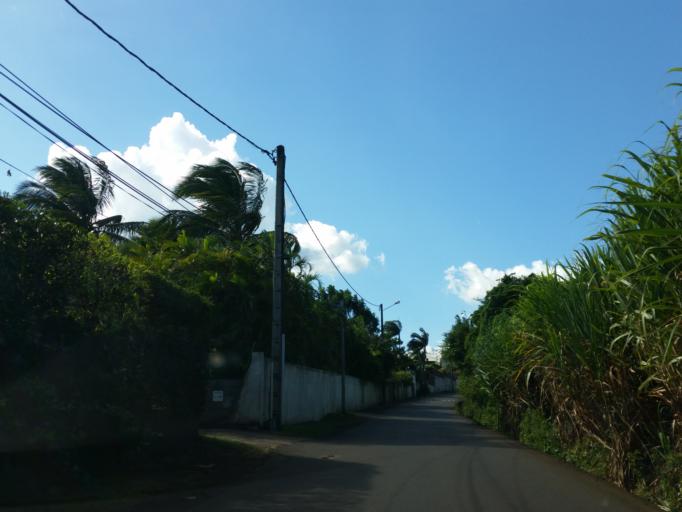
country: RE
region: Reunion
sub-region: Reunion
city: Saint-Pierre
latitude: -21.3276
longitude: 55.4966
